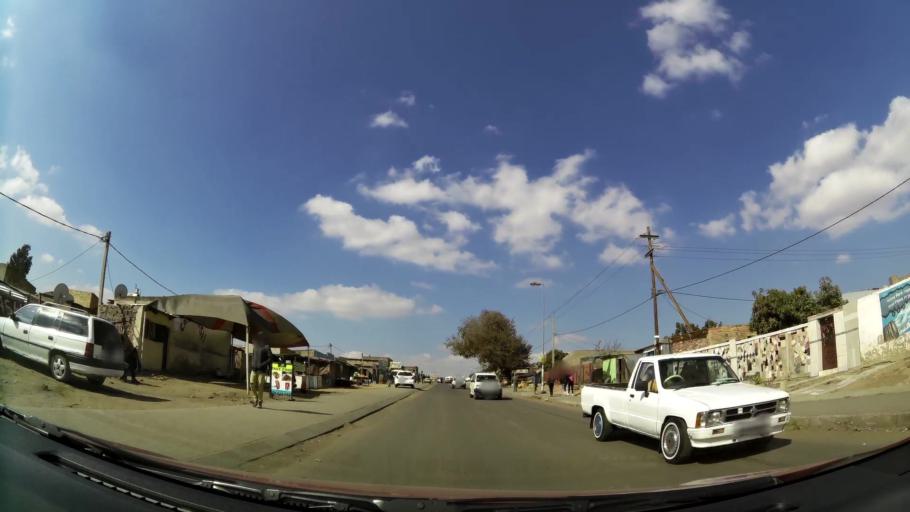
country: ZA
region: Gauteng
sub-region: Ekurhuleni Metropolitan Municipality
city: Tembisa
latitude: -26.0059
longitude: 28.1811
